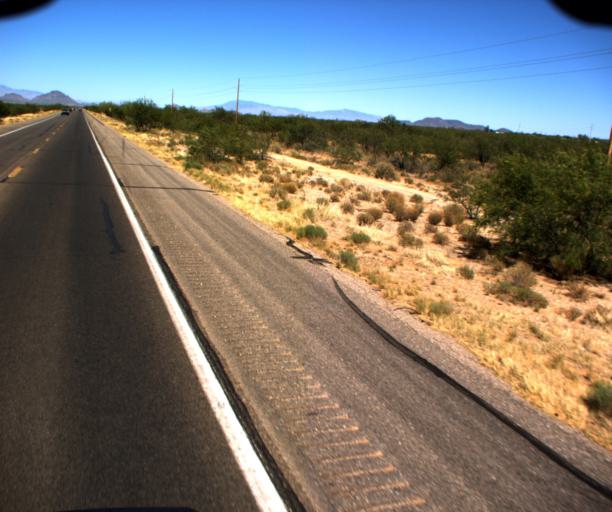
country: US
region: Arizona
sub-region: Pima County
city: Three Points
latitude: 32.1056
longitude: -111.2409
